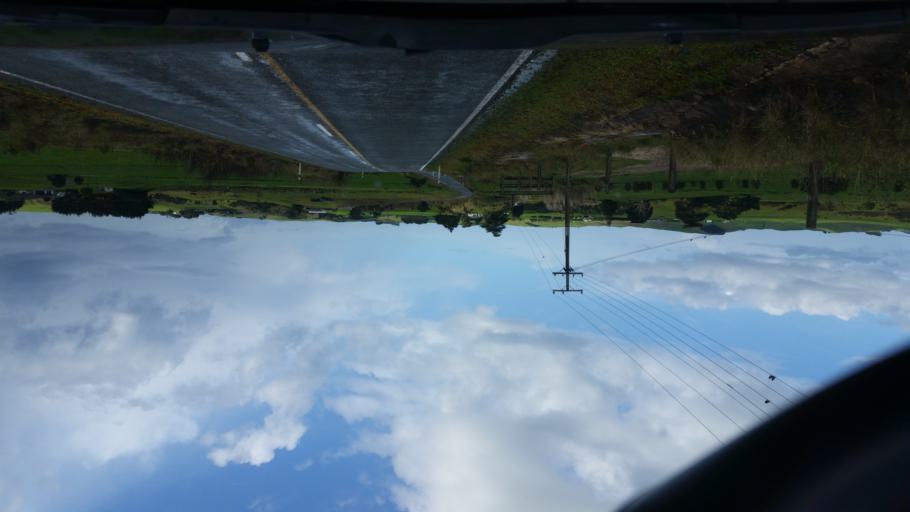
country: NZ
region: Northland
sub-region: Kaipara District
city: Dargaville
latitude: -35.9469
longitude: 173.8102
